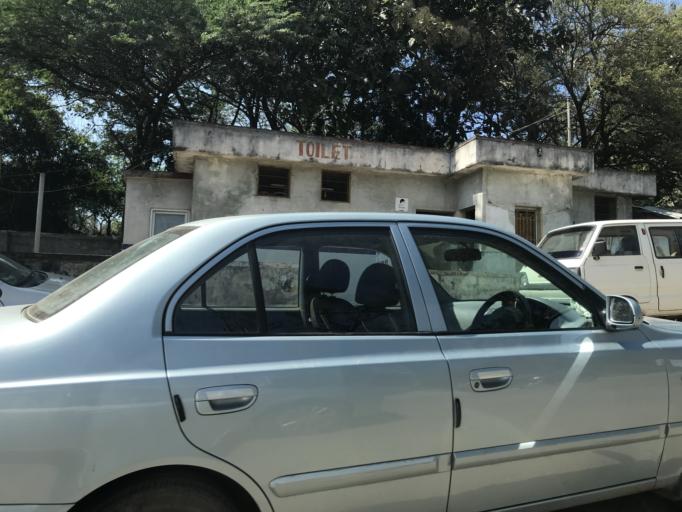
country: IN
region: Karnataka
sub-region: Mysore
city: Heggadadevankote
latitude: 12.0671
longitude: 76.3553
